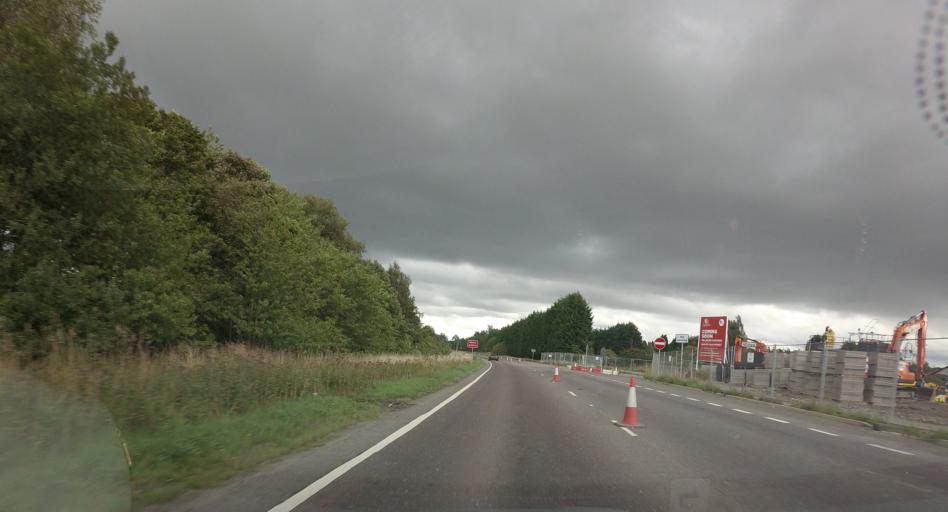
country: GB
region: Scotland
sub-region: Clackmannanshire
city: Clackmannan
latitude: 56.1078
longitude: -3.7413
